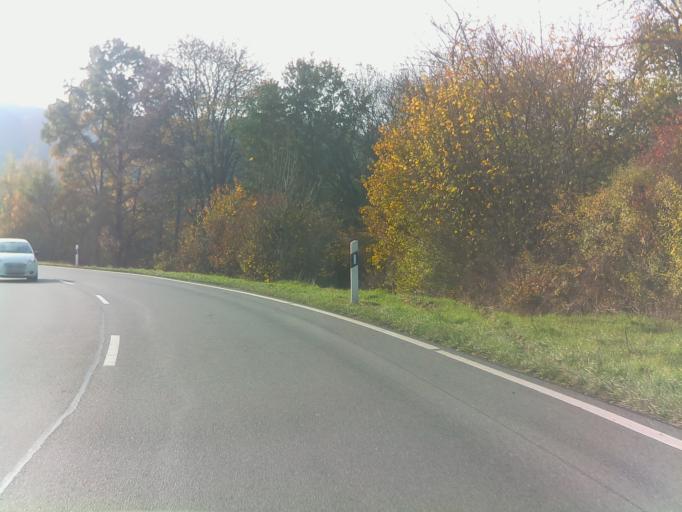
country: DE
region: Baden-Wuerttemberg
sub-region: Karlsruhe Region
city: Adelsheim
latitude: 49.4069
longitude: 9.3544
